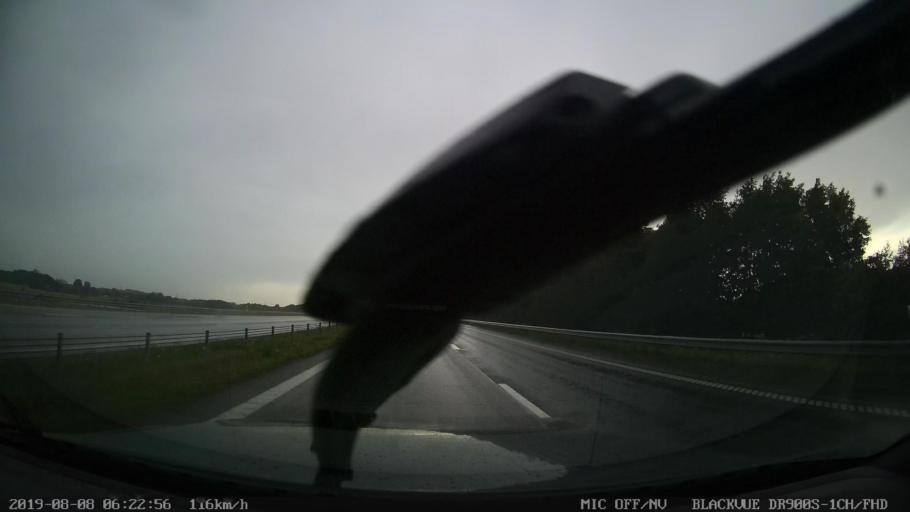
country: SE
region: Skane
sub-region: Helsingborg
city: Odakra
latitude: 56.0870
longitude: 12.7881
